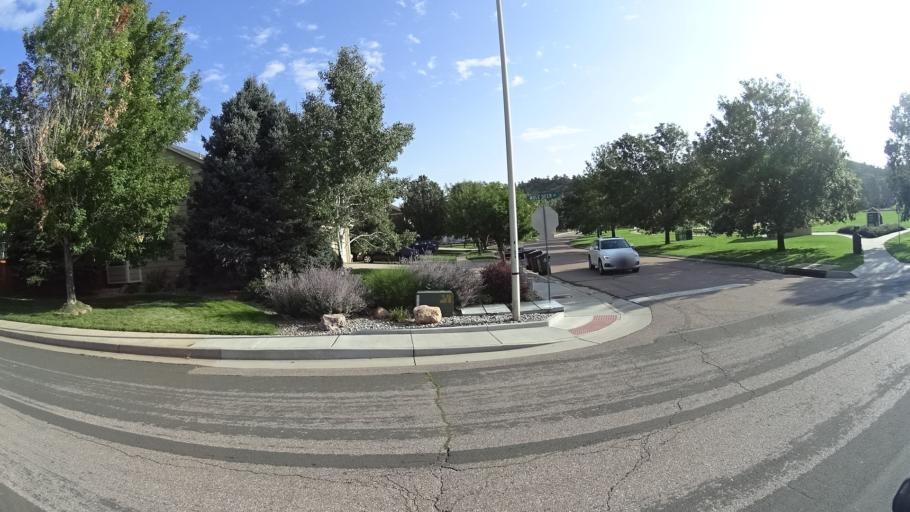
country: US
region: Colorado
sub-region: El Paso County
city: Manitou Springs
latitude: 38.9119
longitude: -104.8612
